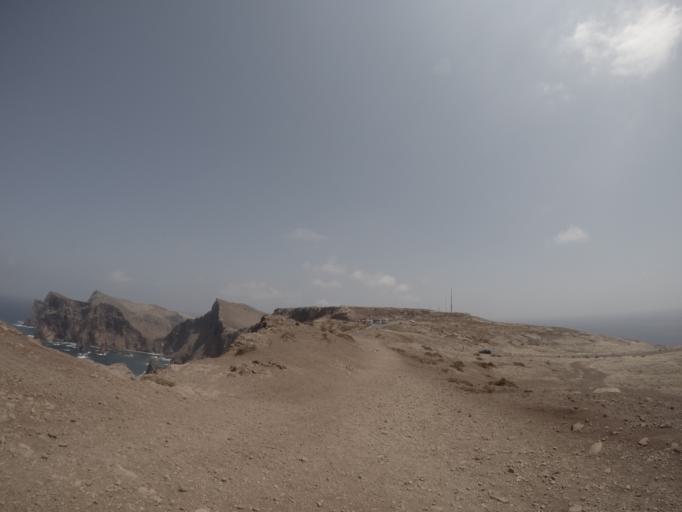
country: PT
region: Madeira
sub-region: Machico
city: Canical
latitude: 32.7505
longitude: -16.7078
